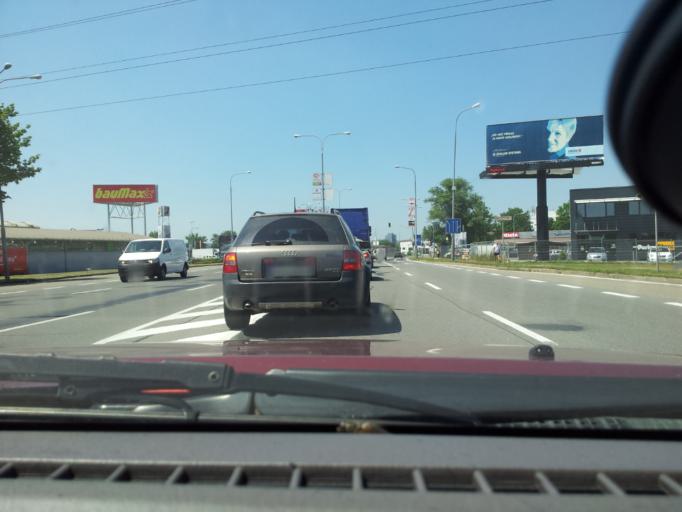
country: CZ
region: South Moravian
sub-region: Mesto Brno
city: Brno
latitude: 49.1661
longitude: 16.6298
